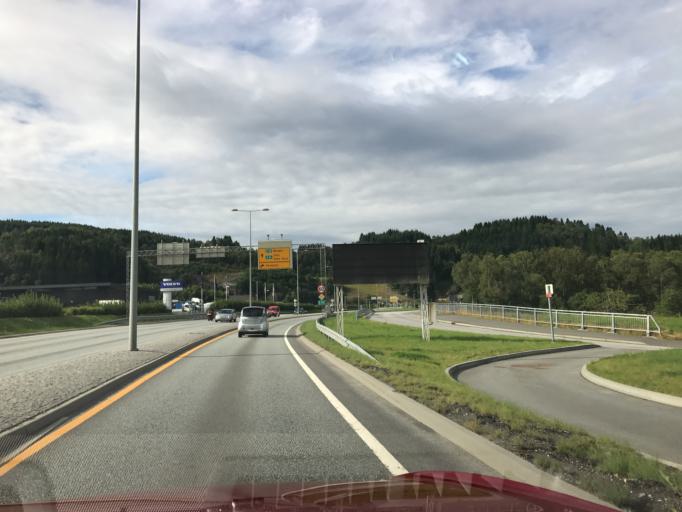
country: NO
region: Hordaland
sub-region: Bergen
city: Hylkje
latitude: 60.4836
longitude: 5.3743
